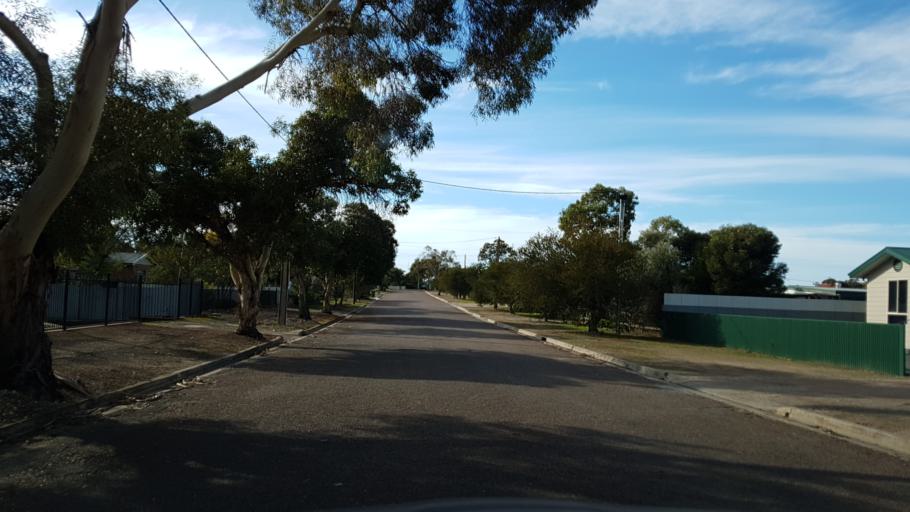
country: AU
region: South Australia
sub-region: Murray Bridge
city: Tailem Bend
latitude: -35.2527
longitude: 139.4600
